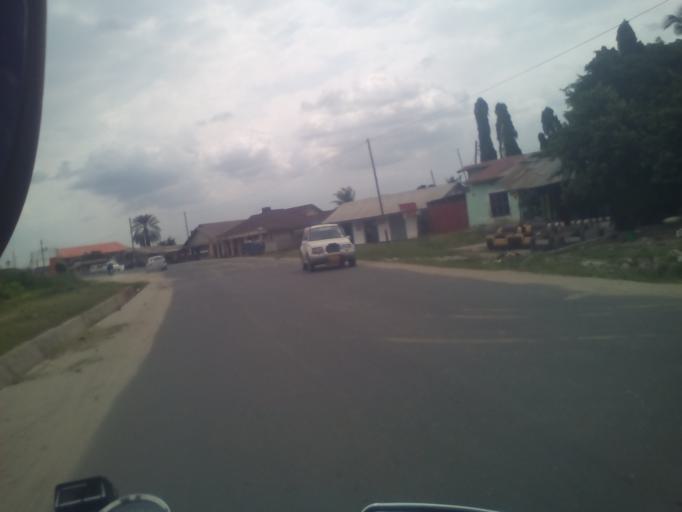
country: TZ
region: Dar es Salaam
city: Dar es Salaam
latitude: -6.8651
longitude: 39.2209
